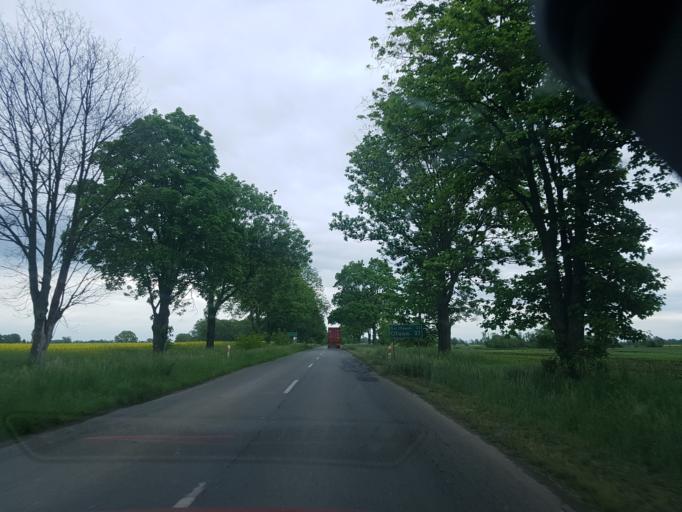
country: PL
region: Lower Silesian Voivodeship
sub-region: Powiat wroclawski
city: Kobierzyce
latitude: 50.9173
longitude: 16.9662
